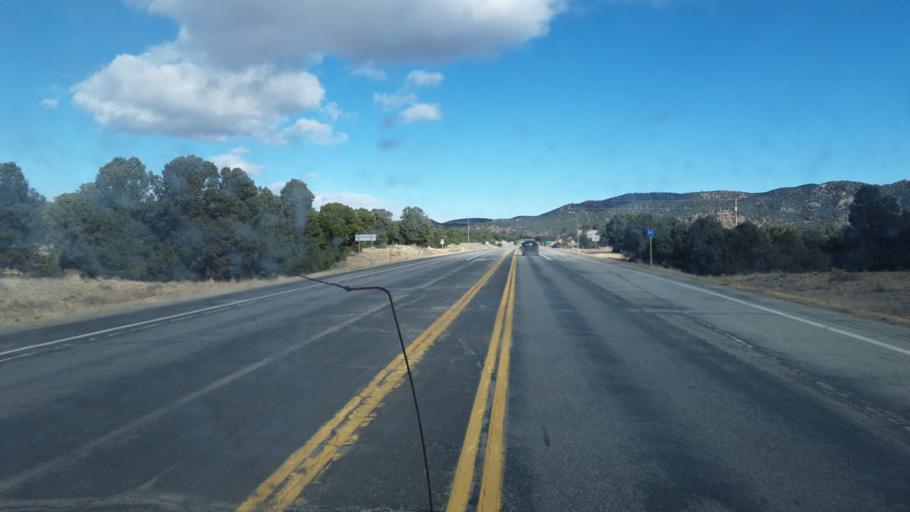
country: US
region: Colorado
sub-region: Chaffee County
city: Salida
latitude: 38.6166
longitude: -106.0795
